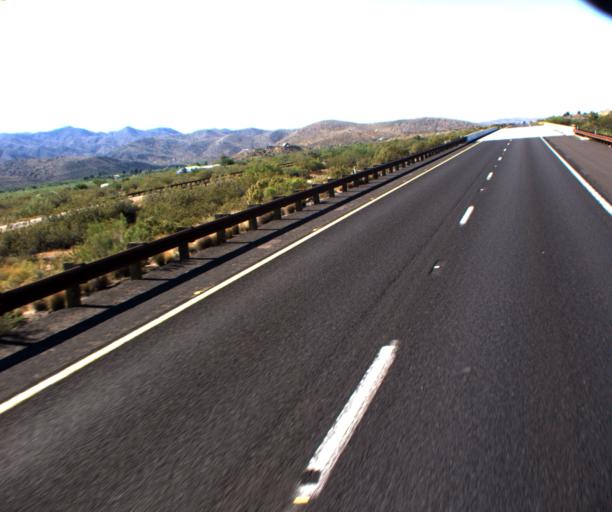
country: US
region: Arizona
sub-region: Mohave County
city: Kingman
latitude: 35.0388
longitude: -113.6652
